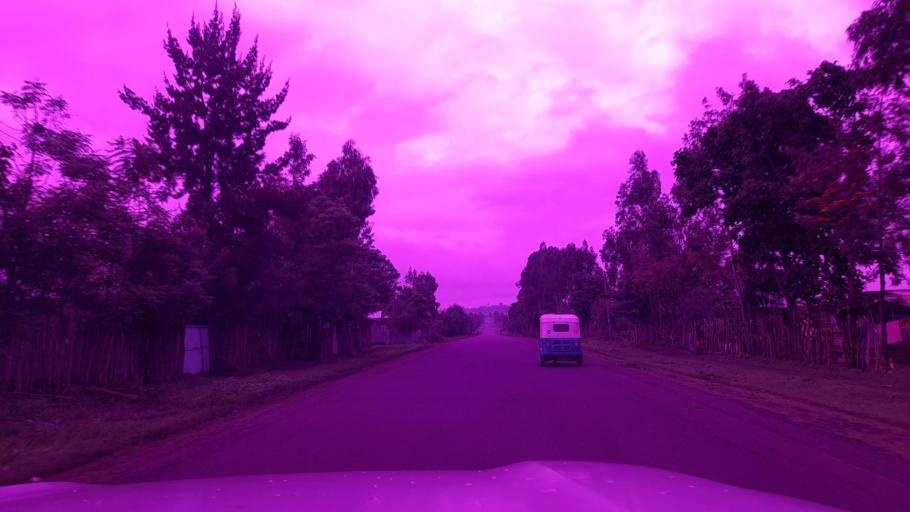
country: ET
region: Oromiya
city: Waliso
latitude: 8.2806
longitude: 37.6894
